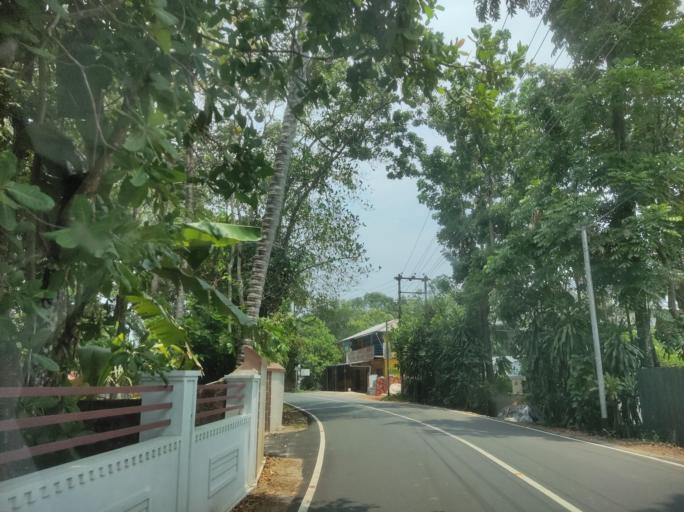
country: IN
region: Kerala
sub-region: Alappuzha
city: Vayalar
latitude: 9.7145
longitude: 76.3274
